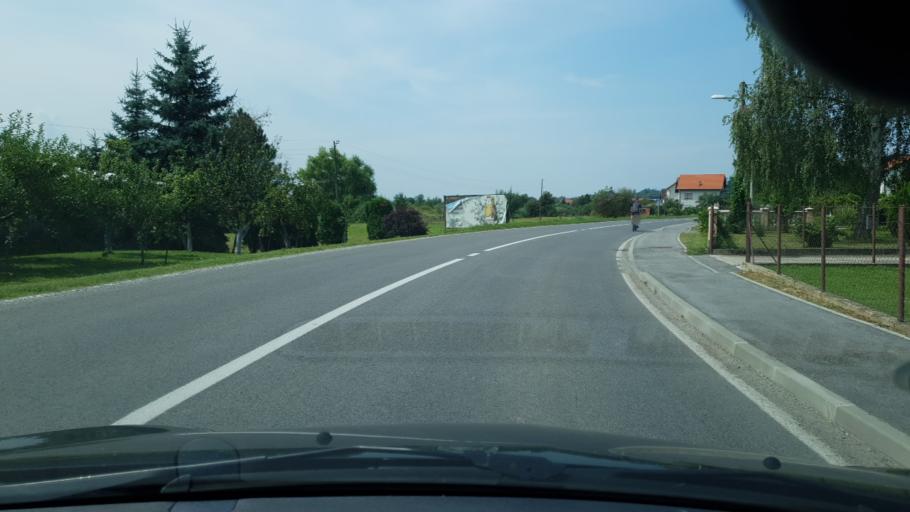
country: HR
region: Krapinsko-Zagorska
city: Bedekovcina
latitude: 46.0360
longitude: 15.9784
